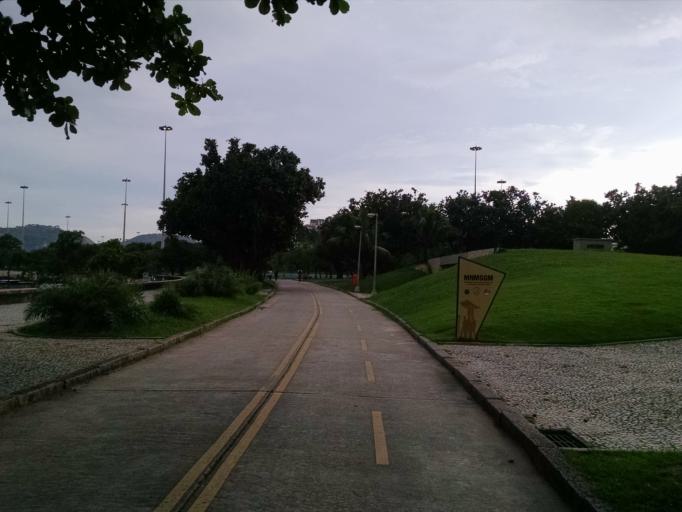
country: BR
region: Rio de Janeiro
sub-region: Rio De Janeiro
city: Rio de Janeiro
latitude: -22.9153
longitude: -43.1749
